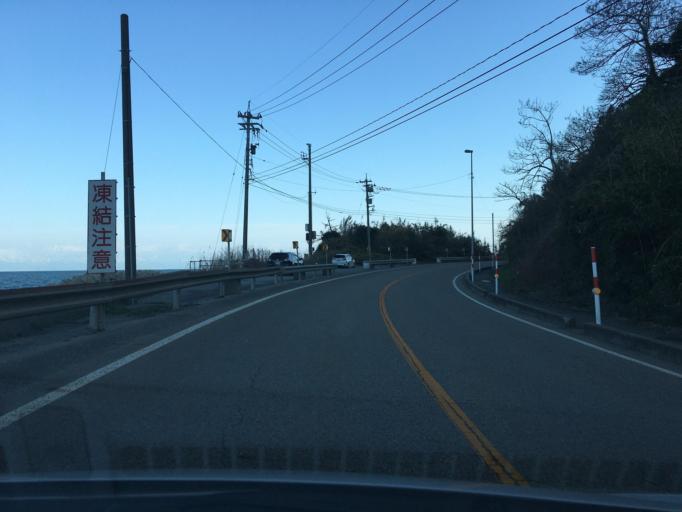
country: JP
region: Ishikawa
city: Nanao
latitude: 36.9952
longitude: 137.0529
